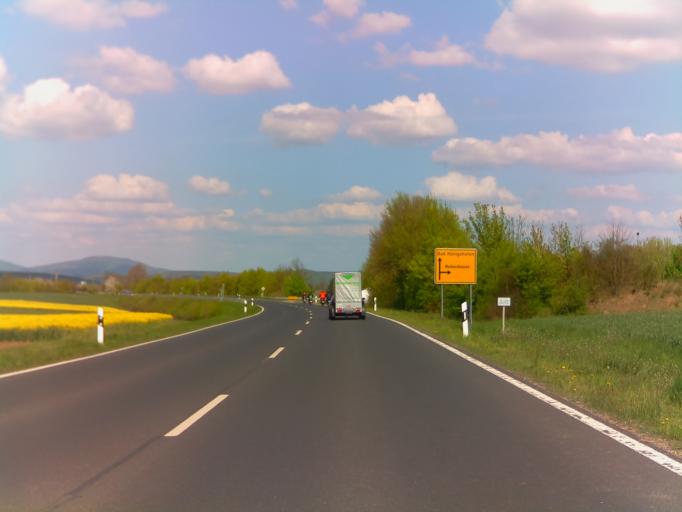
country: DE
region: Bavaria
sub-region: Regierungsbezirk Unterfranken
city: Grosseibstadt
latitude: 50.2841
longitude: 10.4360
